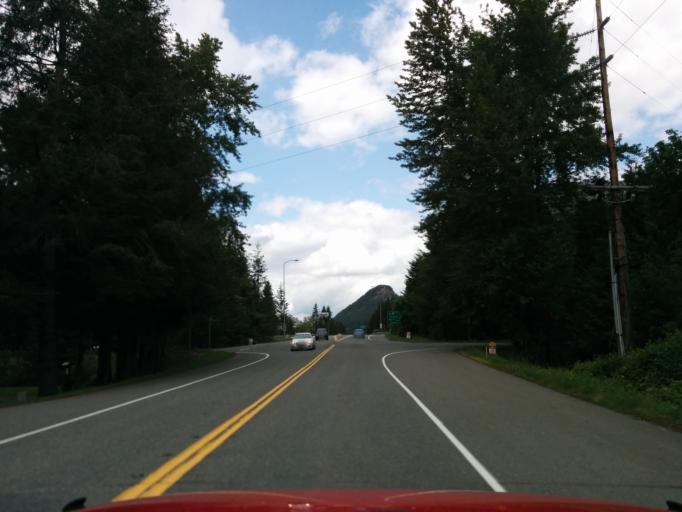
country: US
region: Washington
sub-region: King County
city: Riverbend
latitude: 47.4713
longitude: -121.7584
